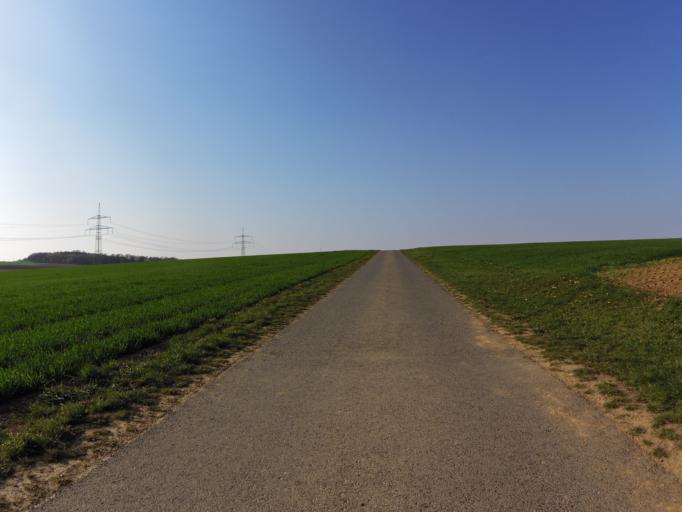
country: DE
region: Bavaria
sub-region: Regierungsbezirk Unterfranken
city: Biebelried
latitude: 49.7693
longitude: 10.0556
